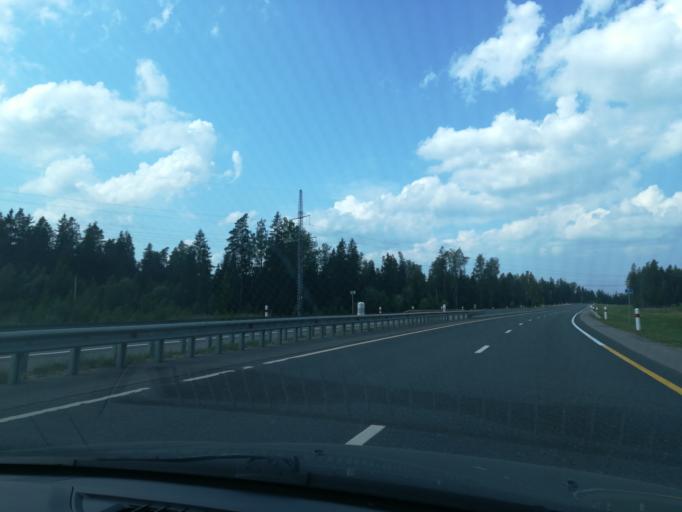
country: RU
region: Leningrad
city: Vistino
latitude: 59.6636
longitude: 28.5311
